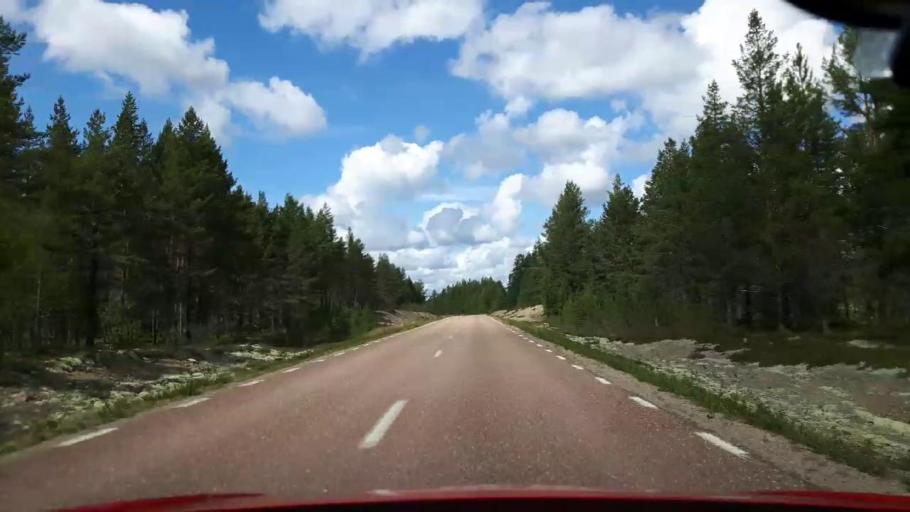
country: SE
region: Dalarna
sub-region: Alvdalens Kommun
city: AElvdalen
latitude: 61.8039
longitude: 13.6568
